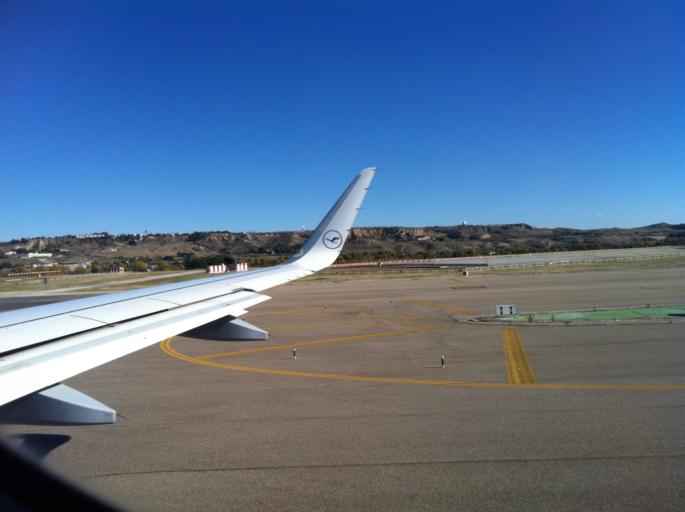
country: ES
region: Madrid
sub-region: Provincia de Madrid
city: Barajas de Madrid
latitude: 40.4971
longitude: -3.5625
